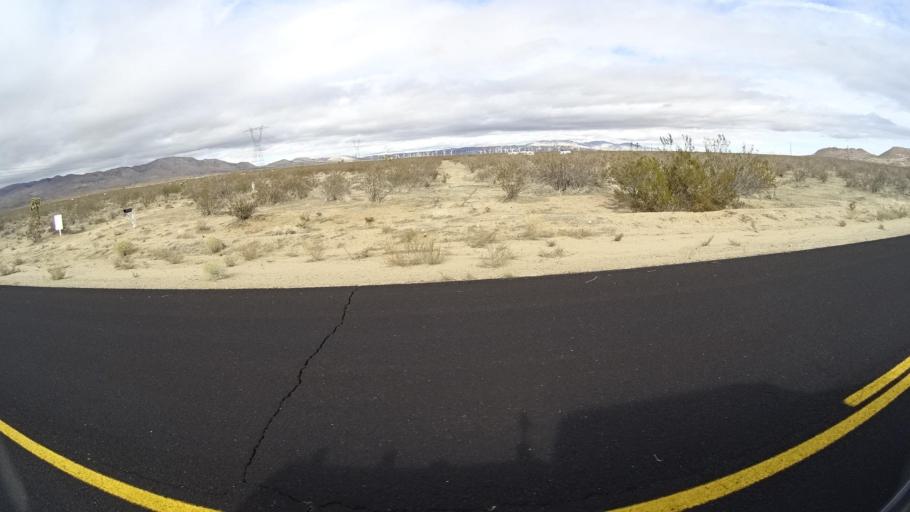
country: US
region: California
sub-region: Kern County
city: Mojave
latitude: 34.9507
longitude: -118.3132
